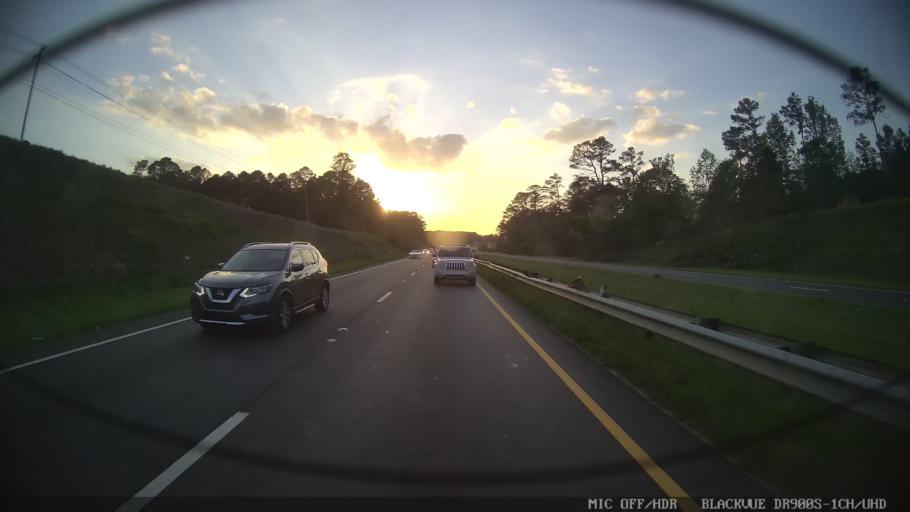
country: US
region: Georgia
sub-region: Cobb County
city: Acworth
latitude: 34.0567
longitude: -84.7148
